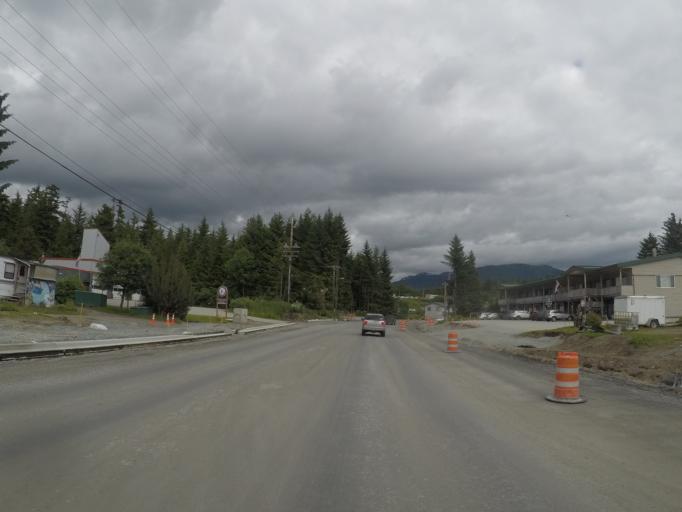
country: US
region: Alaska
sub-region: Juneau City and Borough
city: Juneau
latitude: 58.3874
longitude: -134.6505
